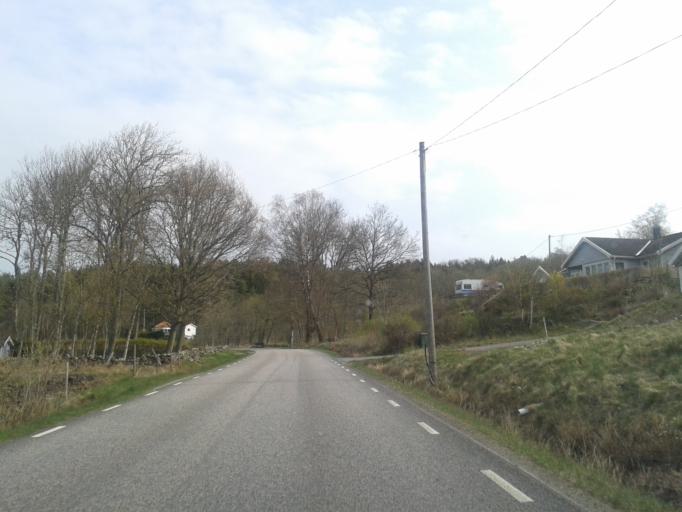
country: SE
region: Vaestra Goetaland
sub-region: Kungalvs Kommun
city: Kode
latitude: 57.9003
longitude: 11.8041
